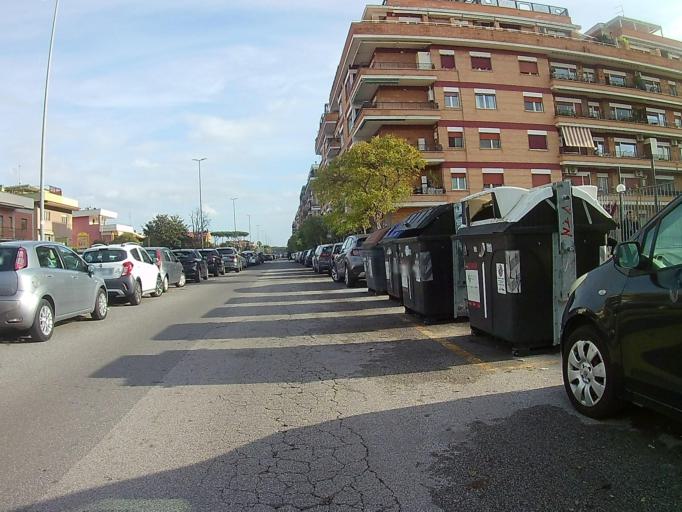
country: IT
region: Latium
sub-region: Citta metropolitana di Roma Capitale
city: Lido di Ostia
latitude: 41.7385
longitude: 12.2885
